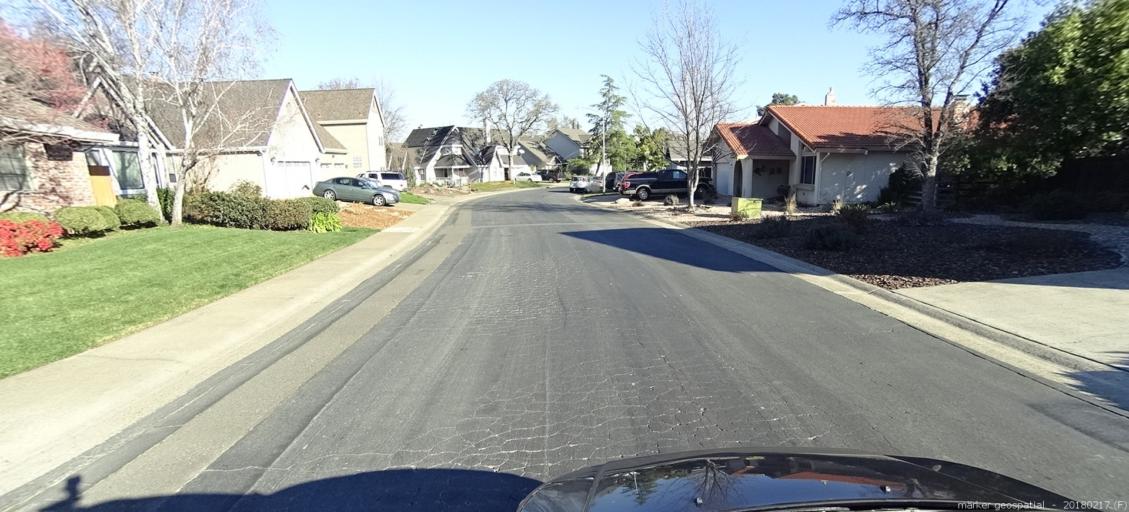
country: US
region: California
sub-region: Sacramento County
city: Folsom
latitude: 38.6688
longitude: -121.1923
